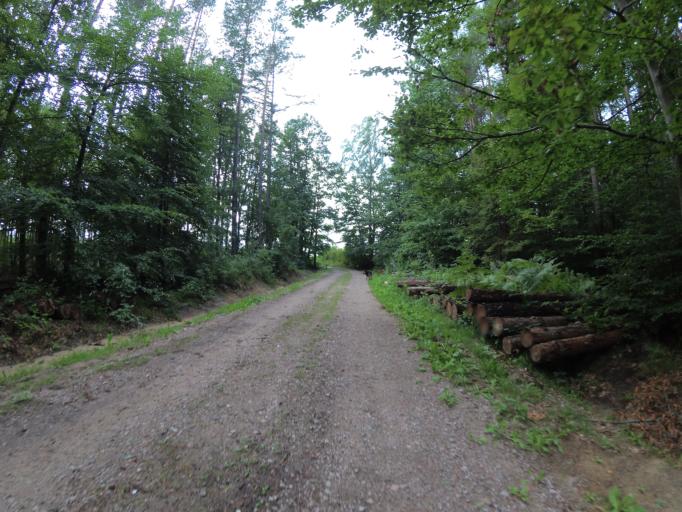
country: PL
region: Pomeranian Voivodeship
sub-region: Powiat wejherowski
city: Bojano
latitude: 54.5072
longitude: 18.4160
